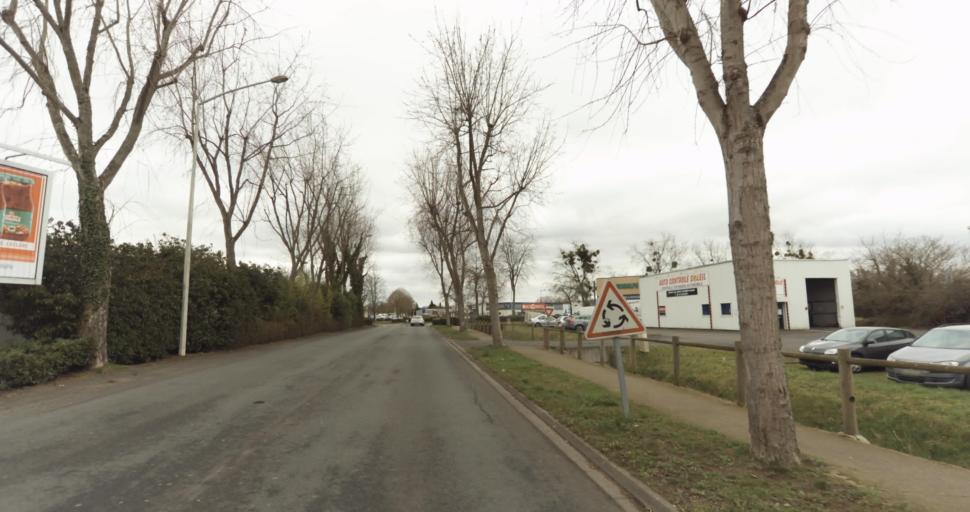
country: FR
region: Pays de la Loire
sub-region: Departement de Maine-et-Loire
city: Saumur
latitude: 47.2758
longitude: -0.0615
